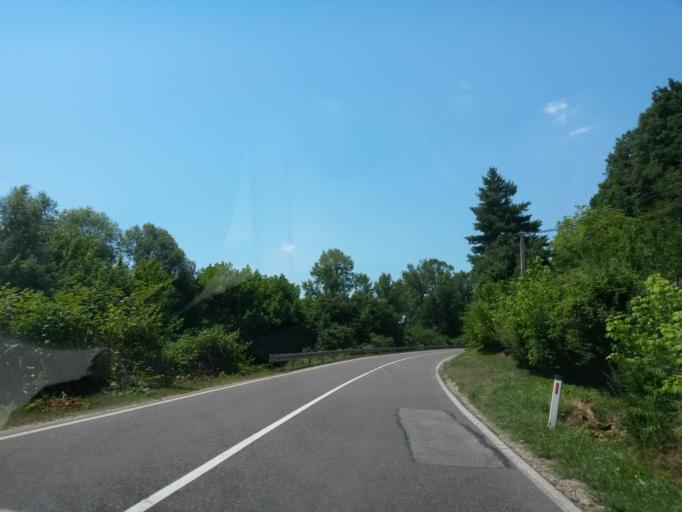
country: BA
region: Federation of Bosnia and Herzegovina
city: Lukavica
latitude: 44.8723
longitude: 18.0817
